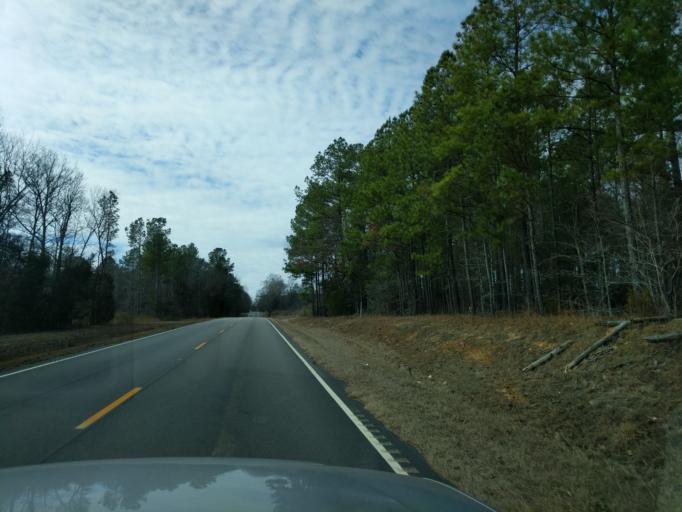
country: US
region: South Carolina
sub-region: Edgefield County
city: Edgefield
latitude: 33.9310
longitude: -81.9892
